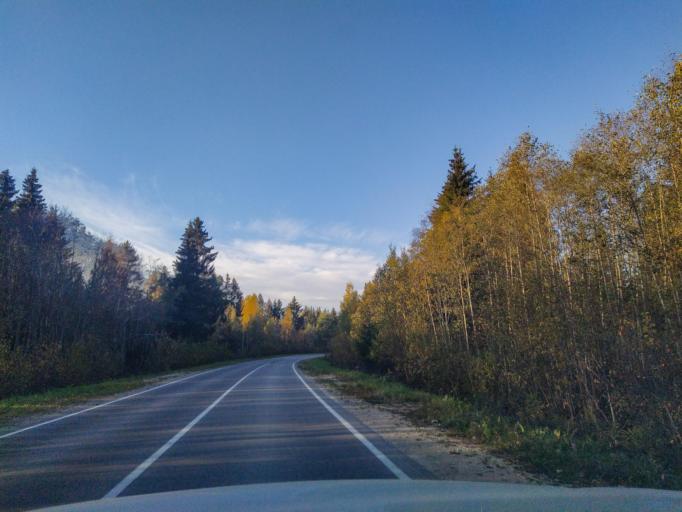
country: RU
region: Leningrad
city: Siverskiy
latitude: 59.3073
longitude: 30.0304
